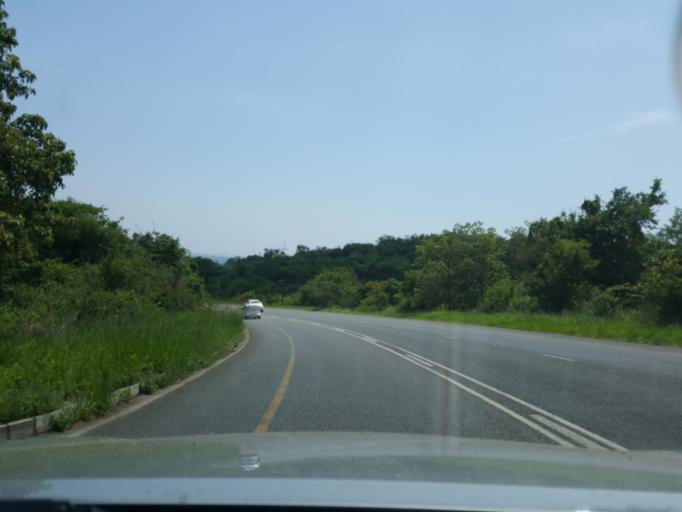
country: ZA
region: Mpumalanga
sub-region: Ehlanzeni District
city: White River
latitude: -25.0708
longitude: 31.1062
